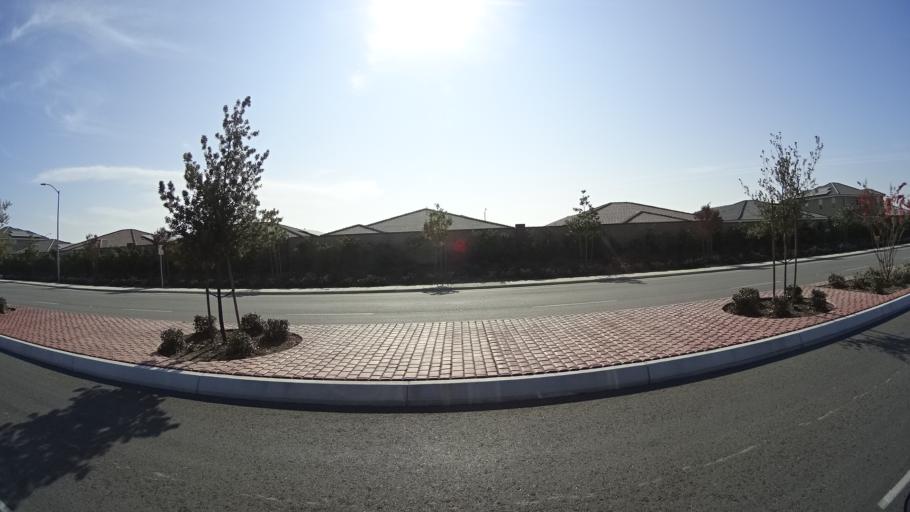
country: US
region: California
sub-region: Kern County
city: Rosedale
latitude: 35.3545
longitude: -119.1717
